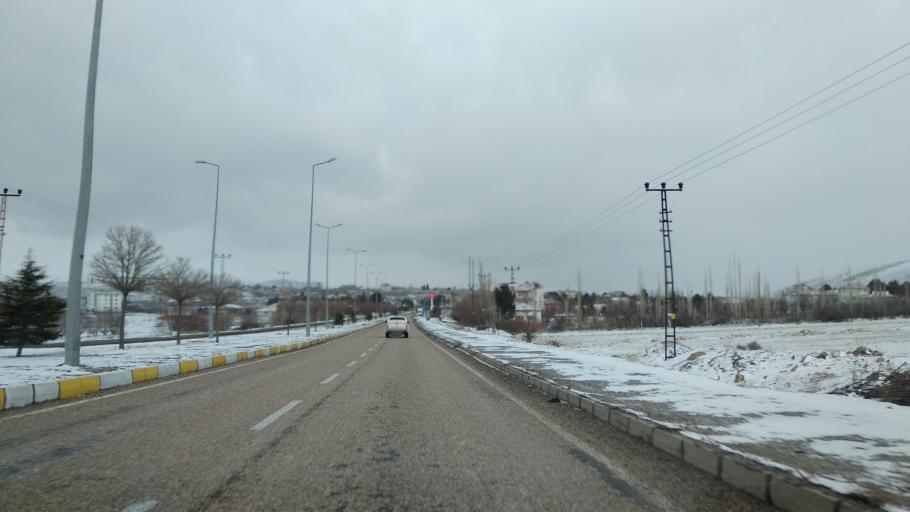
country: TR
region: Kayseri
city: Pinarbasi
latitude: 38.7159
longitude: 36.3822
